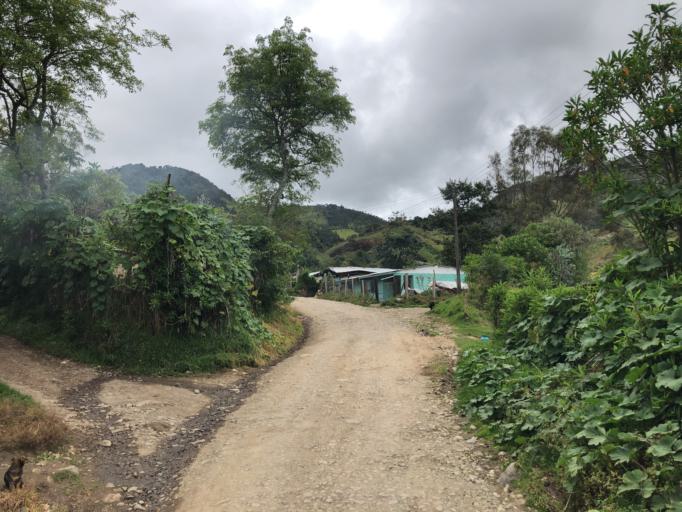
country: CO
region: Cauca
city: Totoro
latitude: 2.5098
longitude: -76.3708
